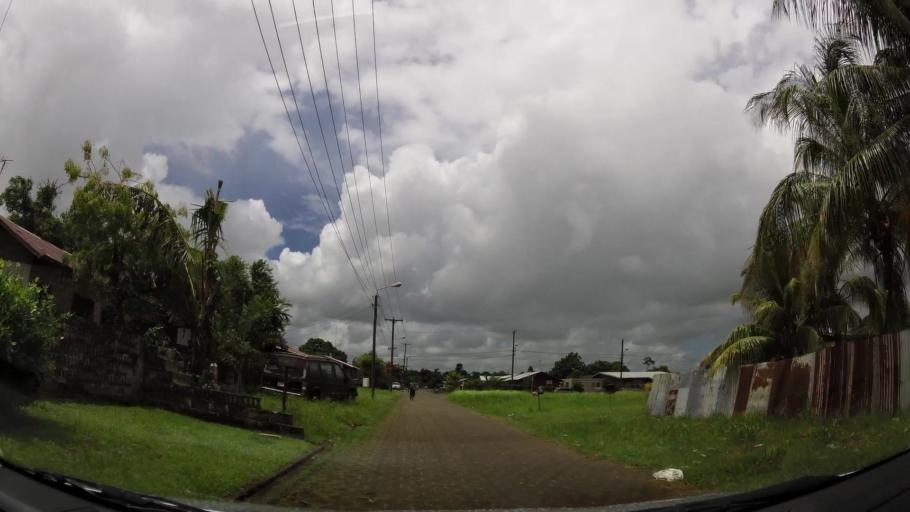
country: SR
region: Paramaribo
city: Paramaribo
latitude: 5.8277
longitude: -55.2255
